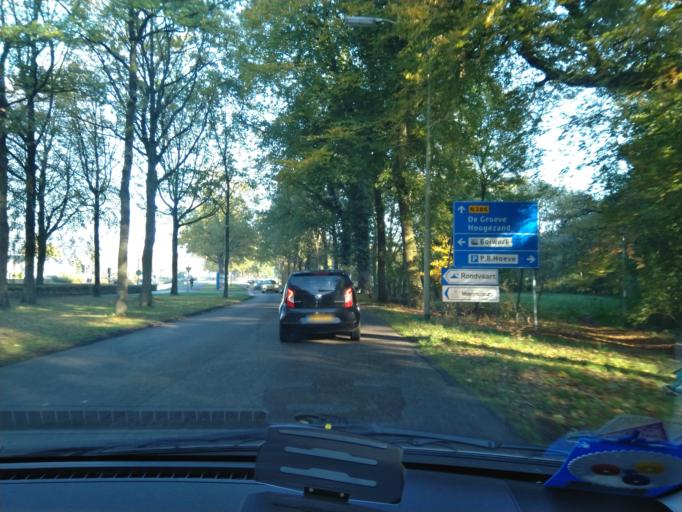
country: NL
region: Drenthe
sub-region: Gemeente Tynaarlo
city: Zuidlaren
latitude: 53.0970
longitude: 6.6901
